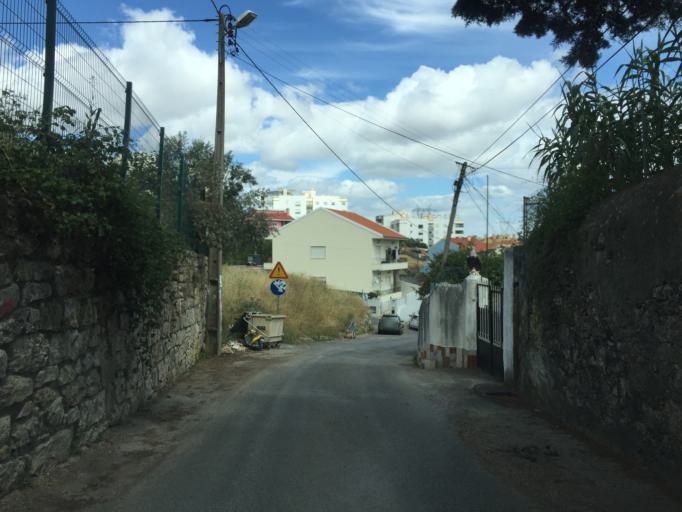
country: PT
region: Lisbon
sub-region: Odivelas
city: Famoes
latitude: 38.7901
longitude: -9.2299
